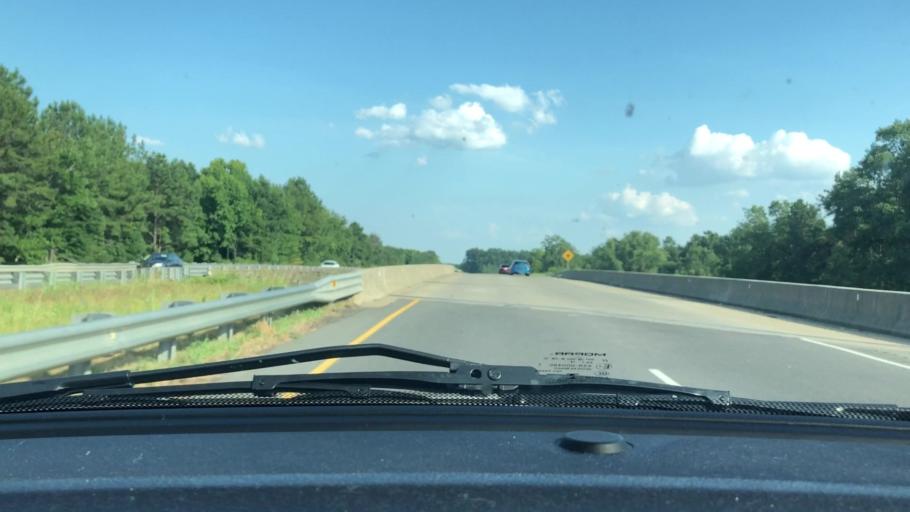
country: US
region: North Carolina
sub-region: Chatham County
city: Farmville
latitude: 35.5662
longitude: -79.2989
